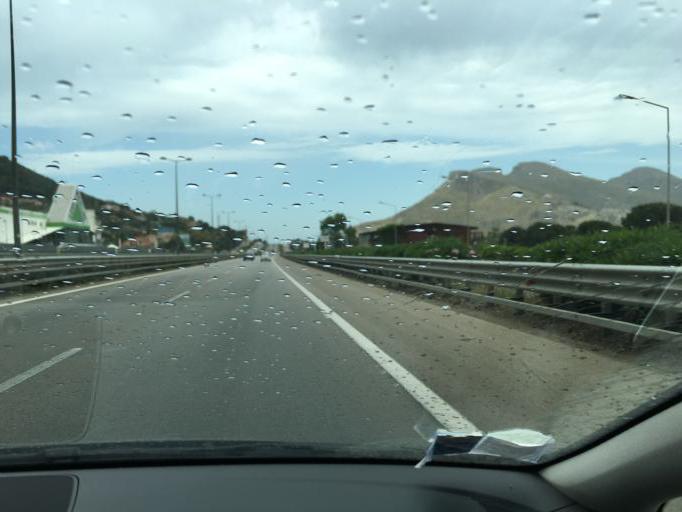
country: IT
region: Sicily
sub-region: Palermo
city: Isola delle Femmine
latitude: 38.1772
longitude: 13.2946
